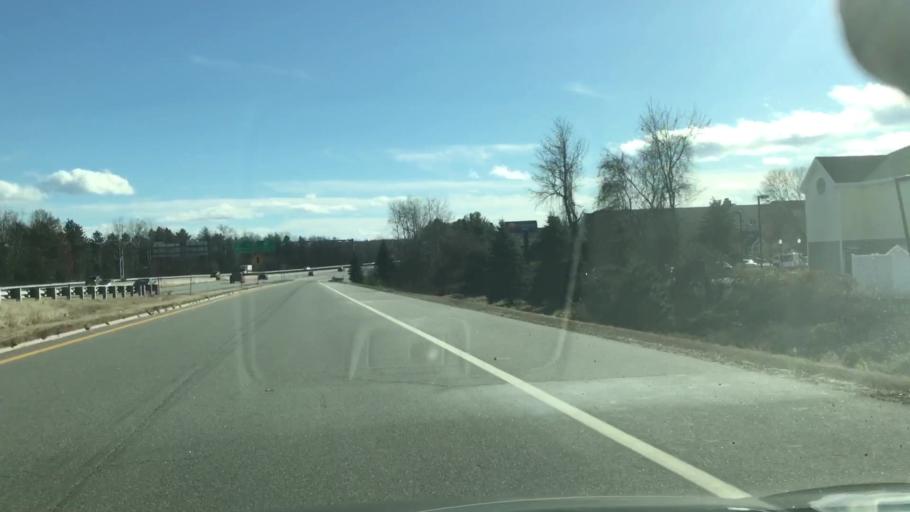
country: US
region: New Hampshire
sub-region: Merrimack County
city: Concord
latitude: 43.1901
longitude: -71.5244
